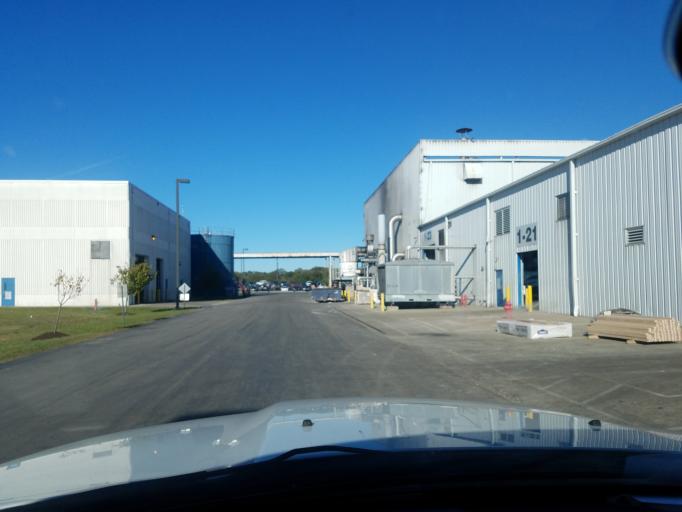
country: US
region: Kentucky
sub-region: Laurel County
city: North Corbin
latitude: 37.0342
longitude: -84.0670
